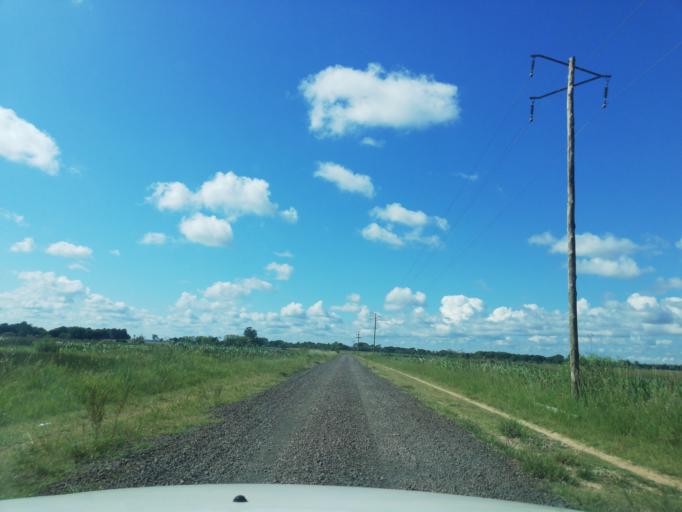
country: AR
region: Corrientes
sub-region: Departamento de San Miguel
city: San Miguel
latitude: -27.9755
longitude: -57.5809
